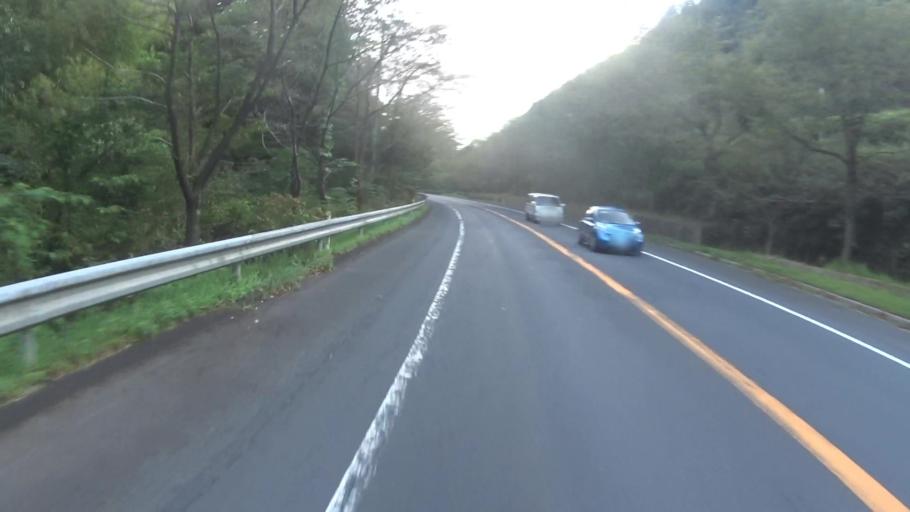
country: JP
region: Kyoto
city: Miyazu
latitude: 35.5475
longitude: 135.1107
